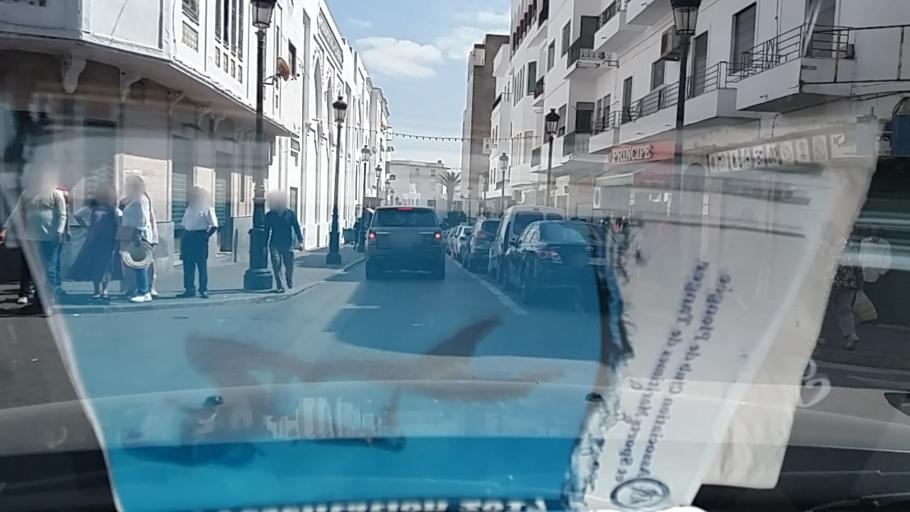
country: MA
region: Tanger-Tetouan
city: Tetouan
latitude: 35.5695
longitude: -5.3733
